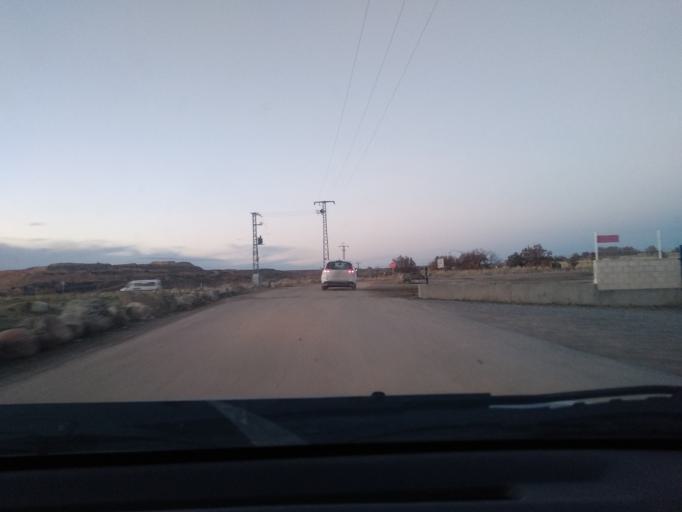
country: ES
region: Castille and Leon
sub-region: Provincia de Segovia
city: San Cristobal de Segovia
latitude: 40.9718
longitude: -4.0830
